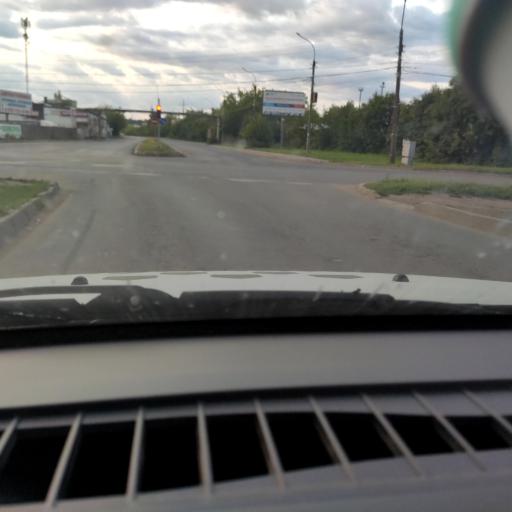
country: RU
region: Kirov
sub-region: Kirovo-Chepetskiy Rayon
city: Kirov
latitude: 58.6156
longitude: 49.6285
